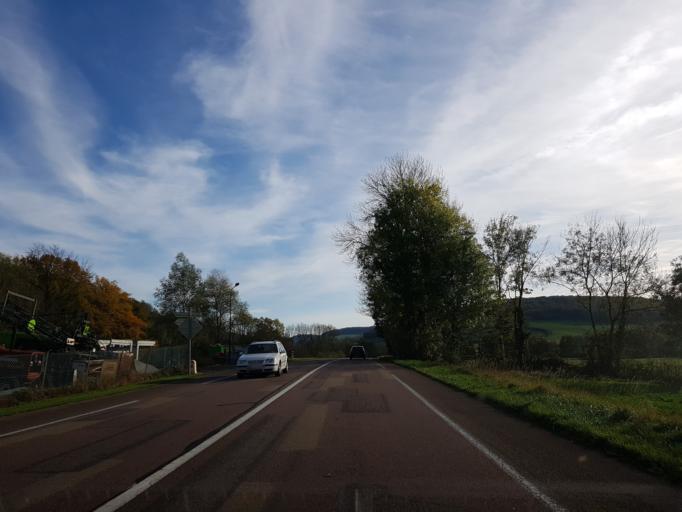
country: FR
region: Bourgogne
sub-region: Departement de la Cote-d'Or
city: Vitteaux
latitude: 47.3682
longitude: 4.5650
